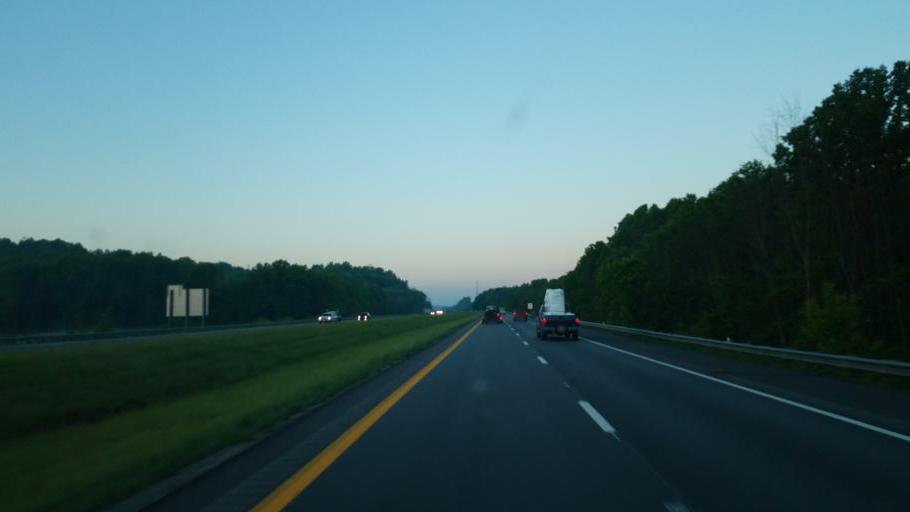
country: US
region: Ohio
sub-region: Guernsey County
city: Byesville
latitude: 39.9602
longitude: -81.5305
